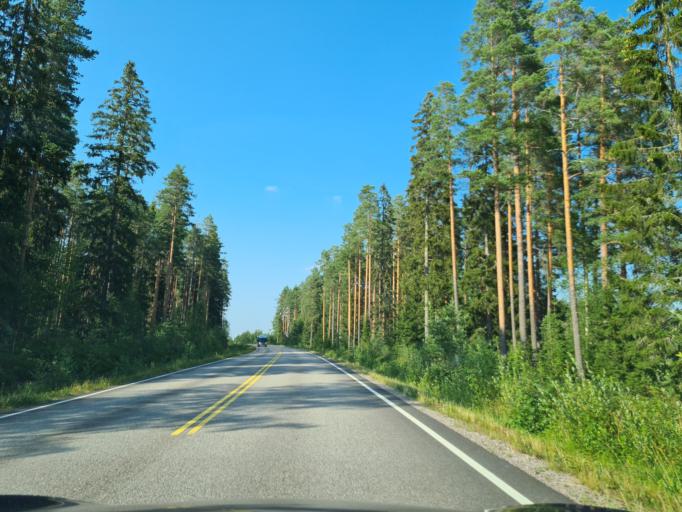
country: FI
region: Satakunta
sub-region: Pohjois-Satakunta
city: Karvia
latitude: 62.2258
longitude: 22.6162
